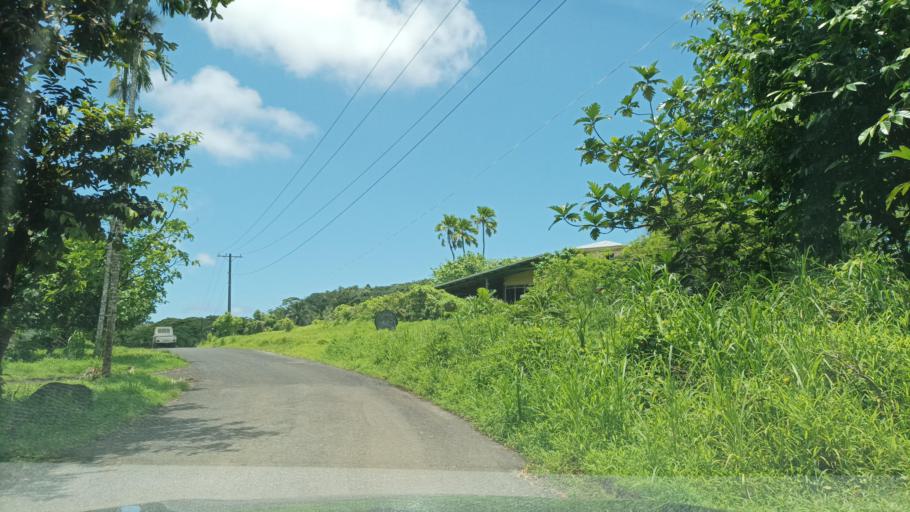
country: FM
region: Pohnpei
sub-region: Madolenihm Municipality
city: Madolenihm Municipality Government
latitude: 6.8427
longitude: 158.3067
